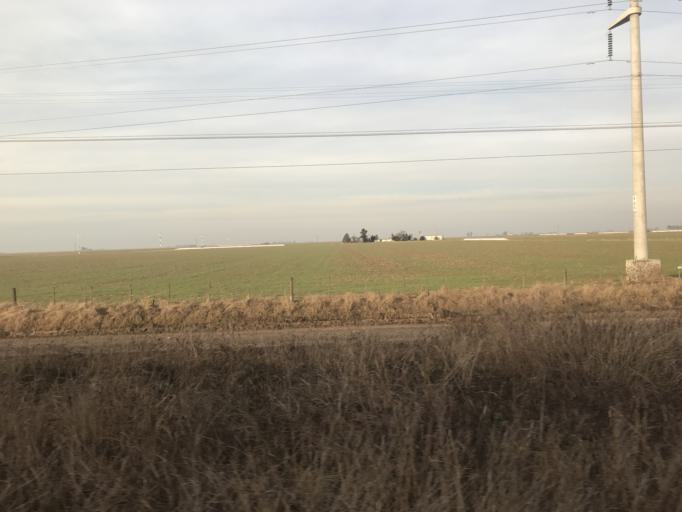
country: AR
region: Cordoba
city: Marcos Juarez
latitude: -32.6842
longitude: -62.1902
